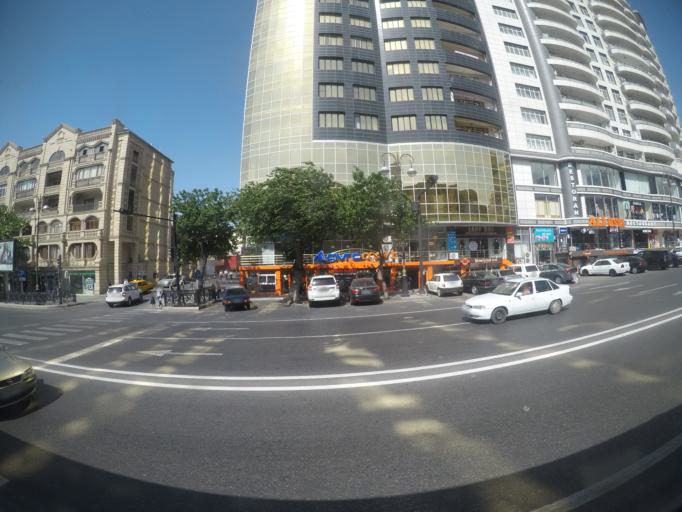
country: AZ
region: Baki
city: Badamdar
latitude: 40.3780
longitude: 49.8318
